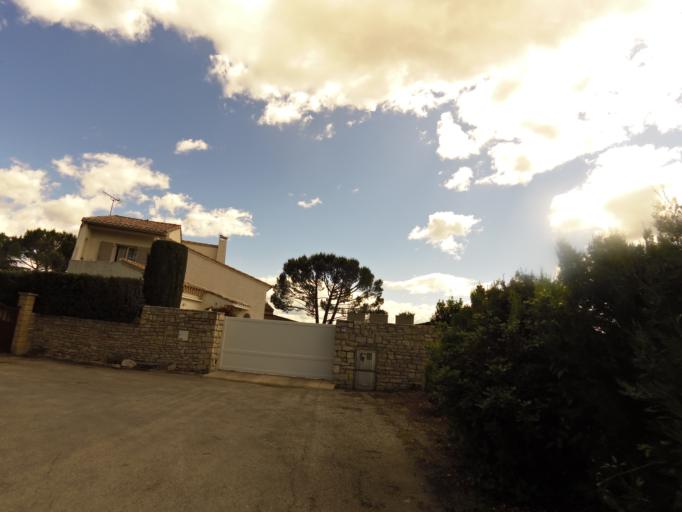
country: FR
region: Languedoc-Roussillon
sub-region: Departement du Gard
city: Calvisson
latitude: 43.7762
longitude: 4.2109
